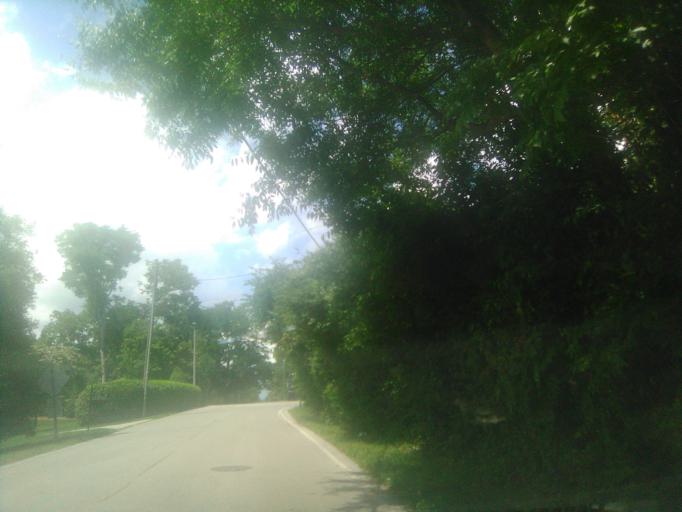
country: US
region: Tennessee
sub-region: Davidson County
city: Belle Meade
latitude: 36.1126
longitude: -86.8482
